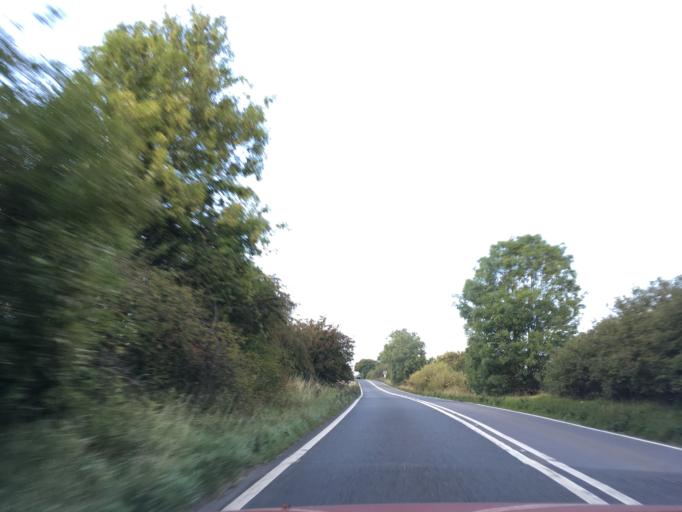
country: GB
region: England
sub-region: Gloucestershire
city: Northleach
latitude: 51.8561
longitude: -1.8029
